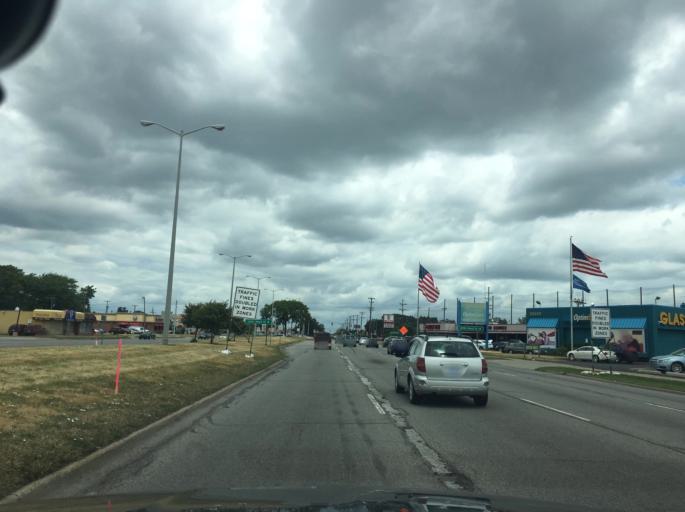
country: US
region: Michigan
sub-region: Macomb County
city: Fraser
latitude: 42.5358
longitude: -82.9114
